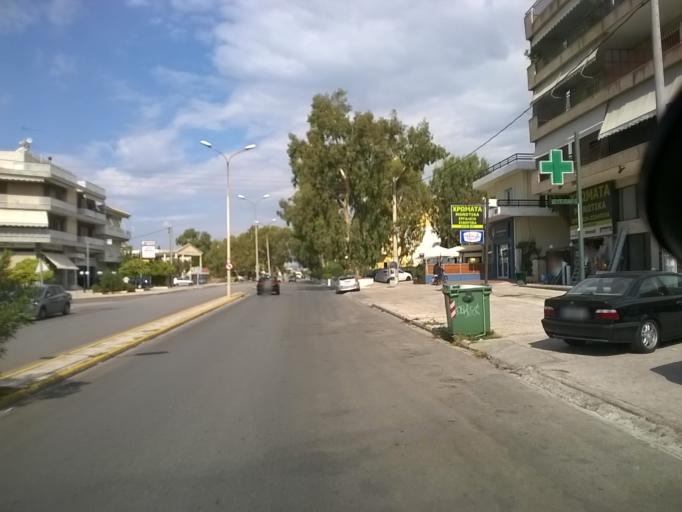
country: GR
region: Attica
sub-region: Nomarchia Athinas
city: Glyfada
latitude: 37.8804
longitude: 23.7573
